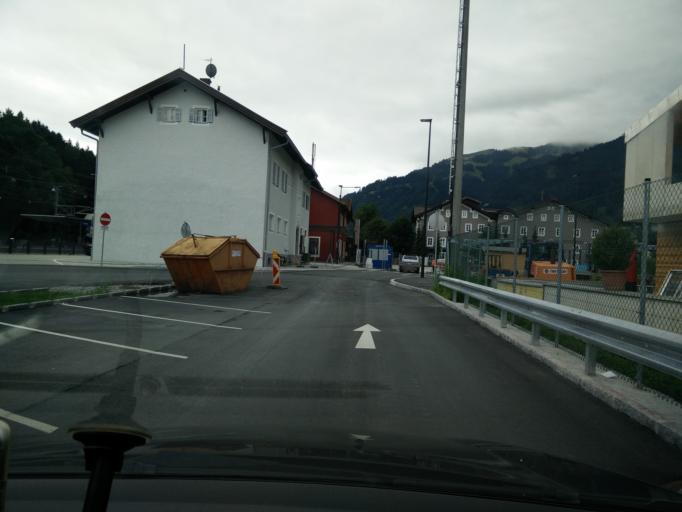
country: AT
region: Tyrol
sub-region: Politischer Bezirk Kitzbuhel
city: Kitzbuhel
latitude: 47.4550
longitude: 12.3903
